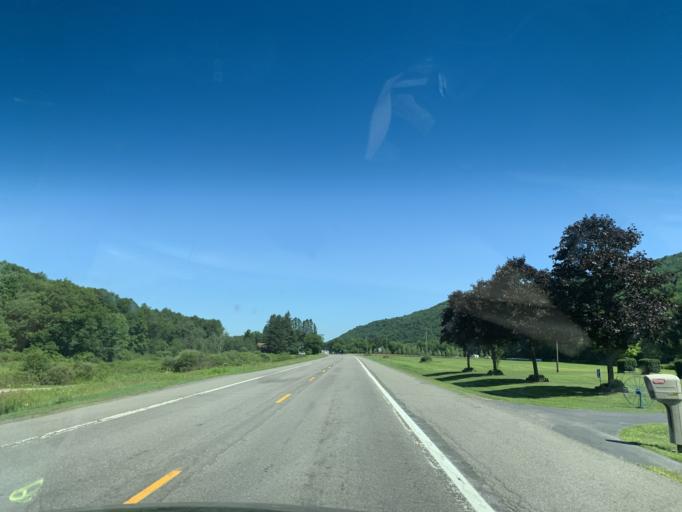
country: US
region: New York
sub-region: Delaware County
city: Sidney
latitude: 42.4400
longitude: -75.3872
